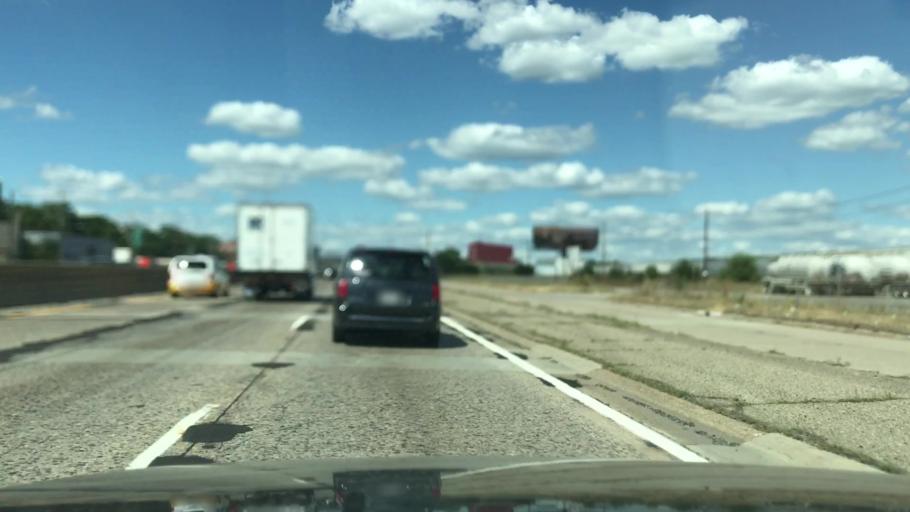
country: US
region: Michigan
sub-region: Kent County
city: Grand Rapids
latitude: 42.9369
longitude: -85.6796
